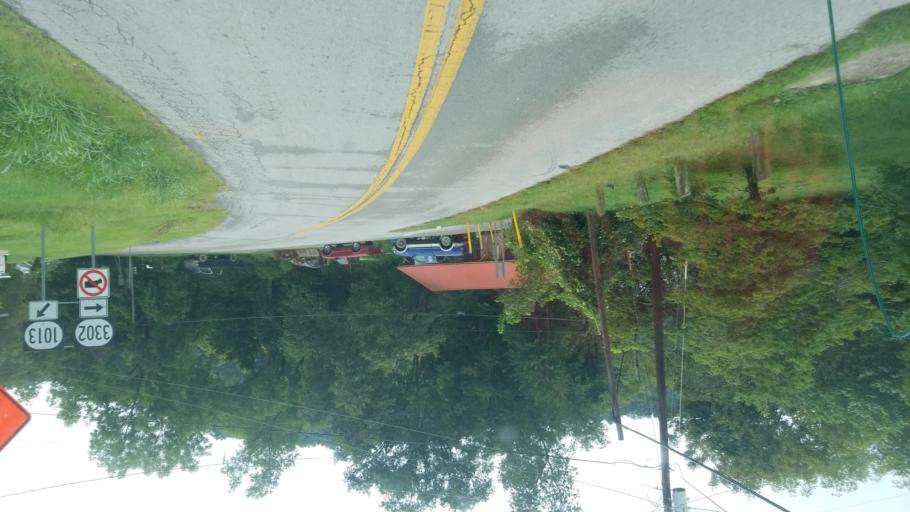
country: US
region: Kentucky
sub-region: Rowan County
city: Morehead
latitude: 38.3507
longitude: -83.5274
